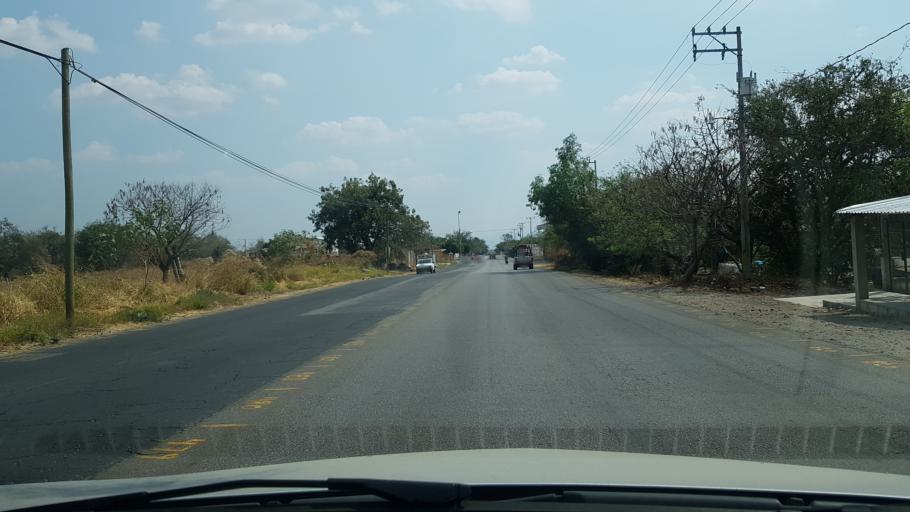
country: MX
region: Morelos
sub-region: Temoac
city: Huazulco
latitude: 18.7488
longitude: -98.7825
